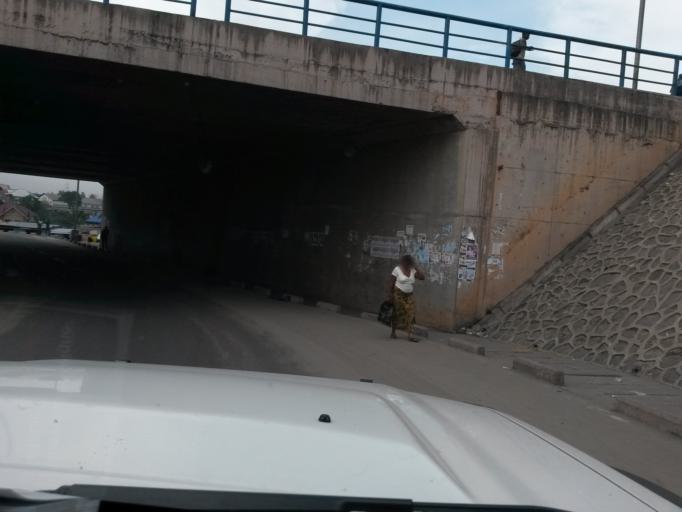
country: CD
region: Kinshasa
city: Masina
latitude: -4.3815
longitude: 15.3508
